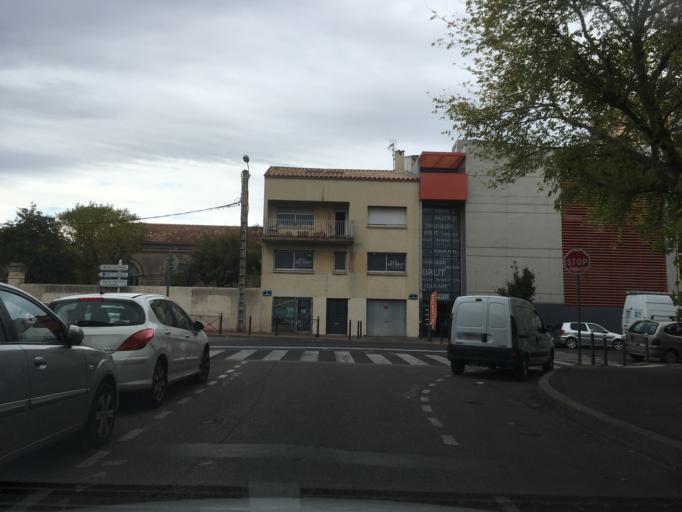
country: FR
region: Languedoc-Roussillon
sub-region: Departement de l'Herault
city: Montpellier
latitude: 43.6181
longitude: 3.8827
